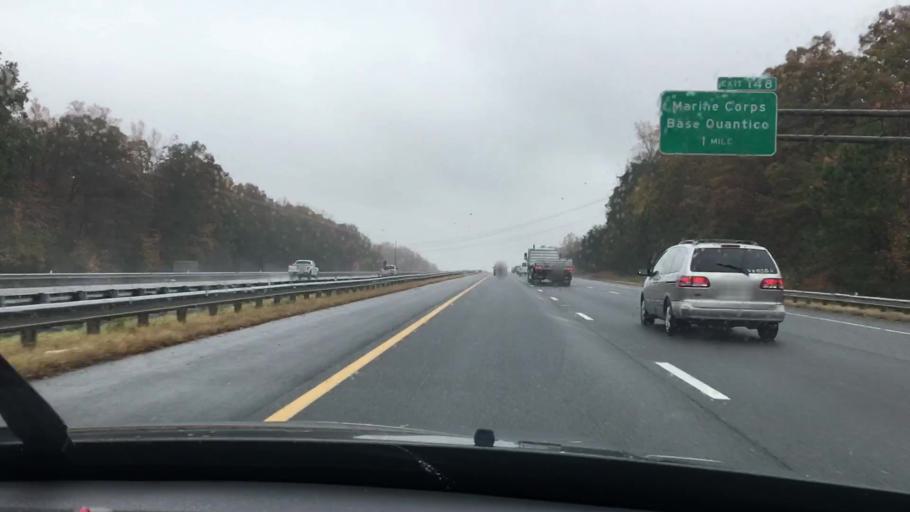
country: US
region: Virginia
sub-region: Prince William County
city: Triangle
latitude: 38.5343
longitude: -77.3560
